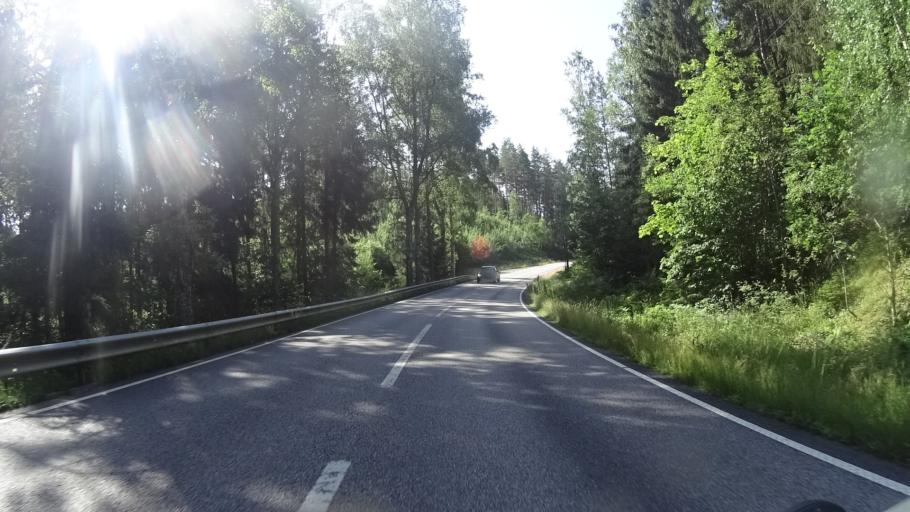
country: SE
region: Kalmar
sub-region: Vasterviks Kommun
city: Overum
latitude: 58.0312
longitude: 16.2368
